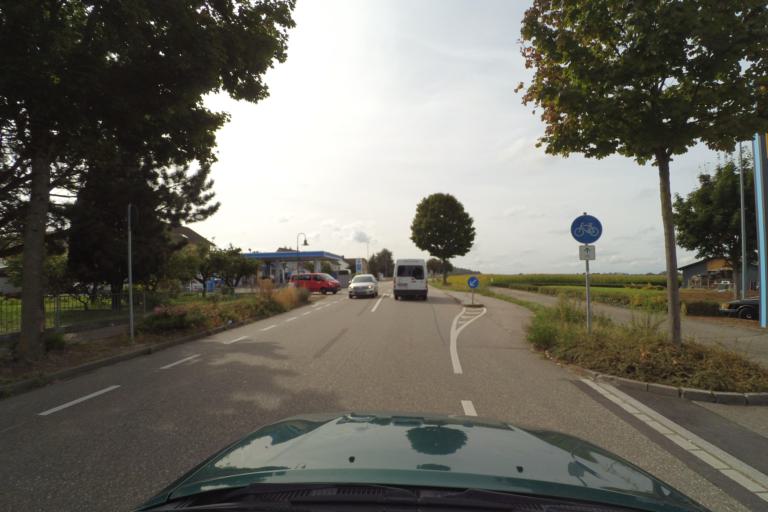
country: DE
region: Baden-Wuerttemberg
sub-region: Freiburg Region
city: Friesenheim
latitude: 48.3711
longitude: 7.8731
